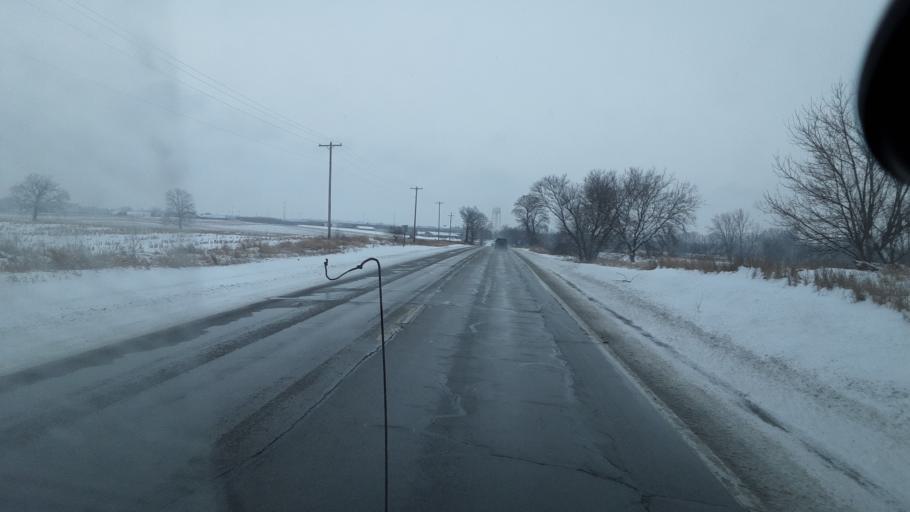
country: US
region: Michigan
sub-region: Jackson County
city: Jackson
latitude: 42.3085
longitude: -84.3886
